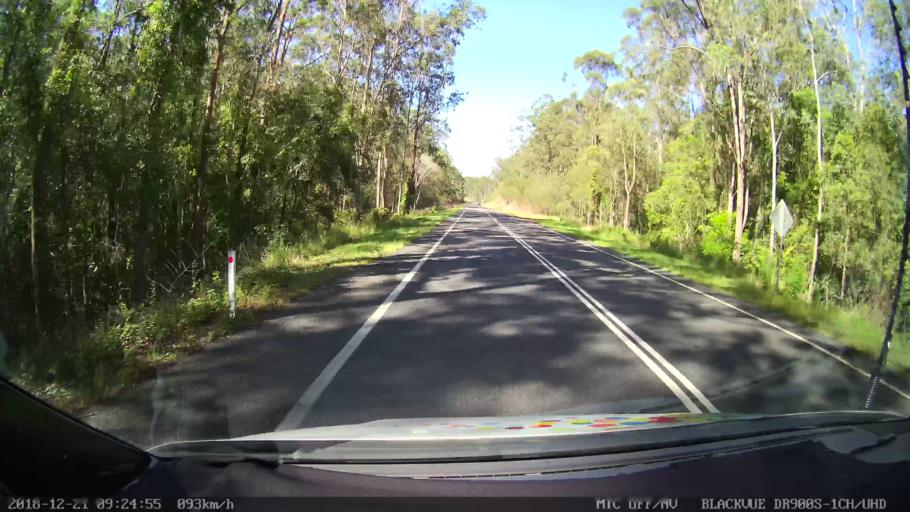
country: AU
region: New South Wales
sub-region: Clarence Valley
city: Maclean
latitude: -29.3733
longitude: 153.0133
